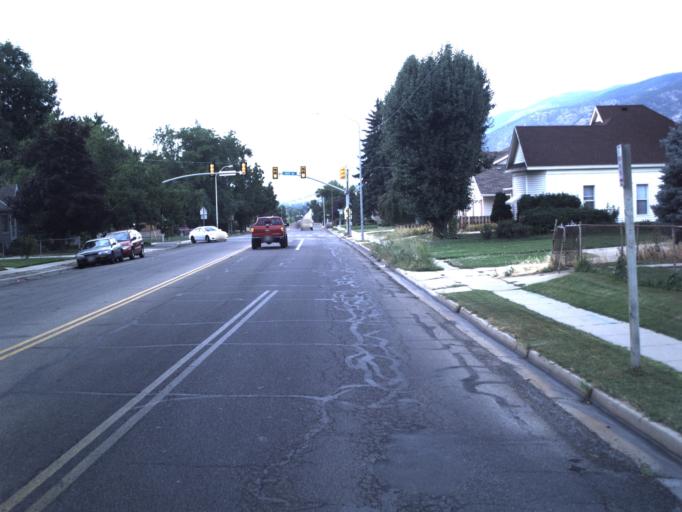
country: US
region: Utah
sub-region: Davis County
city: Bountiful
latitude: 40.8987
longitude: -111.8789
